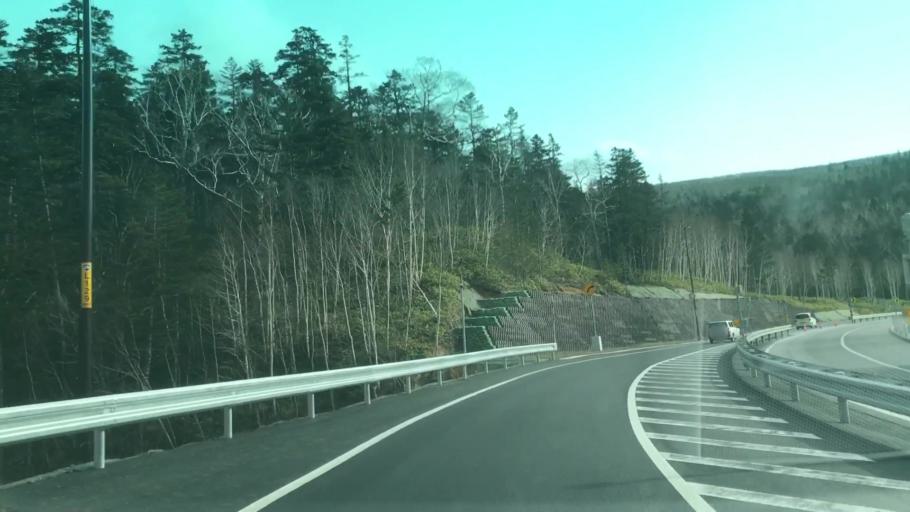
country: JP
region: Hokkaido
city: Otofuke
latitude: 42.9838
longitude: 142.7536
